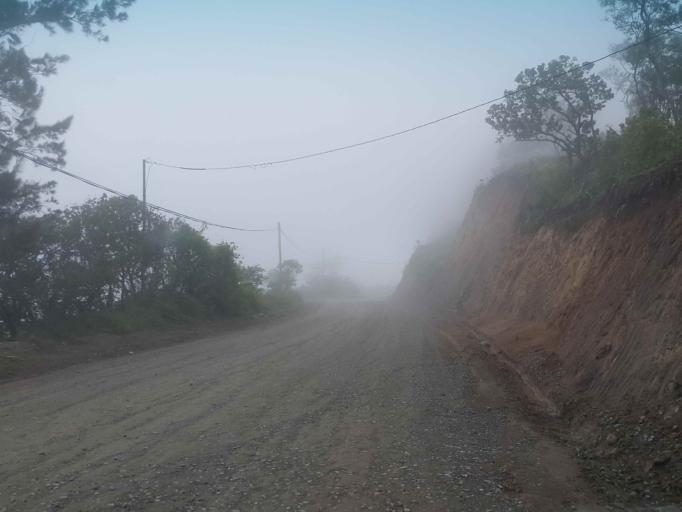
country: CR
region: Guanacaste
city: Juntas
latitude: 10.2945
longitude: -84.8326
